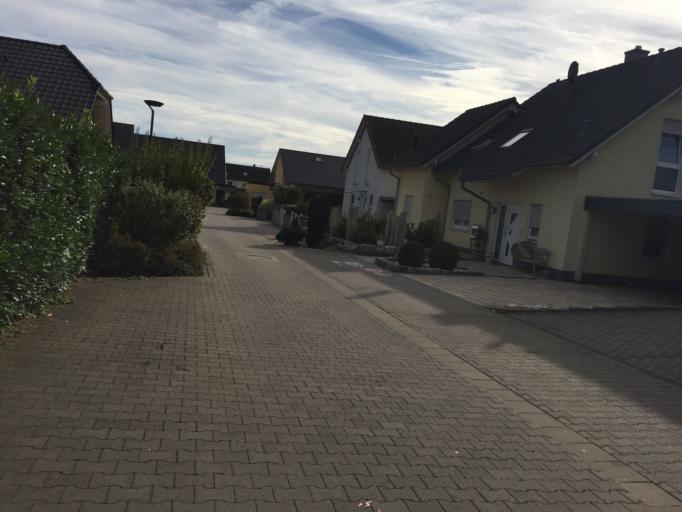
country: DE
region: Hesse
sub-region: Regierungsbezirk Giessen
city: Langgons
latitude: 50.4926
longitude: 8.7233
